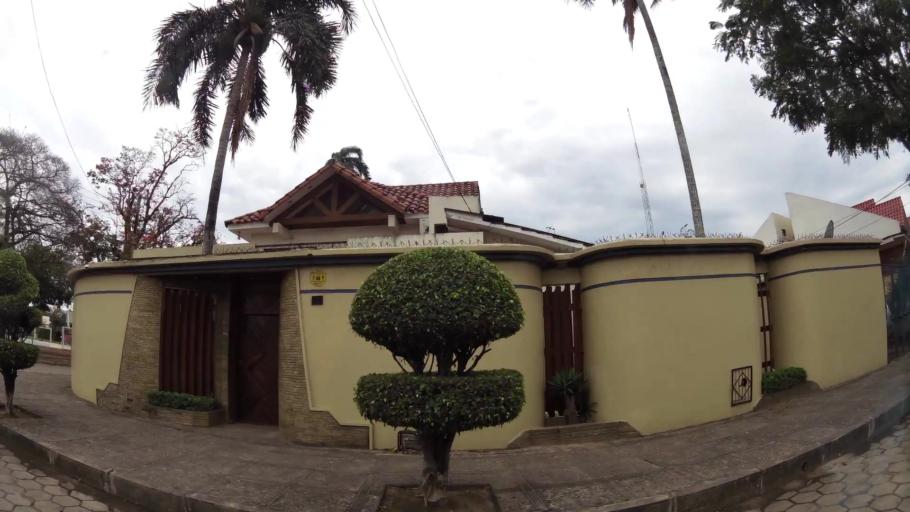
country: BO
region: Santa Cruz
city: Santa Cruz de la Sierra
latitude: -17.7688
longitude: -63.1736
